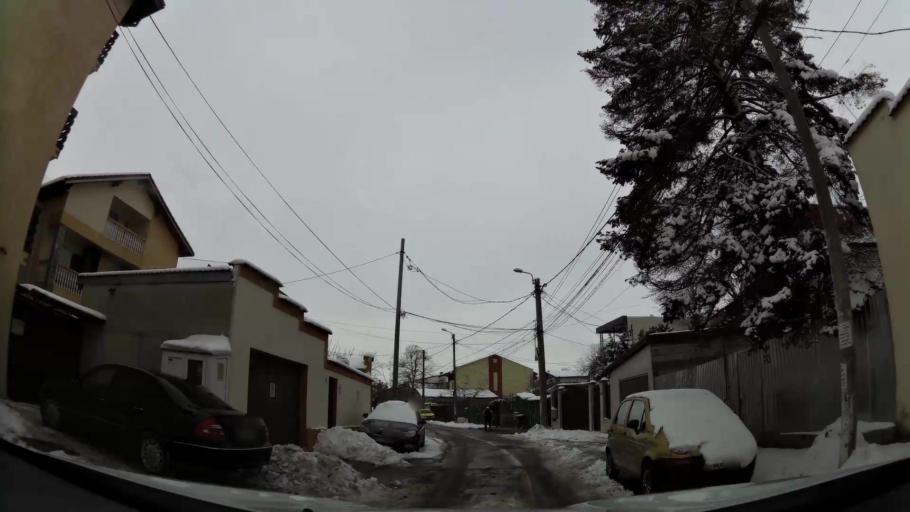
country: RO
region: Bucuresti
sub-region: Municipiul Bucuresti
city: Bucuresti
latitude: 44.3917
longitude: 26.1030
